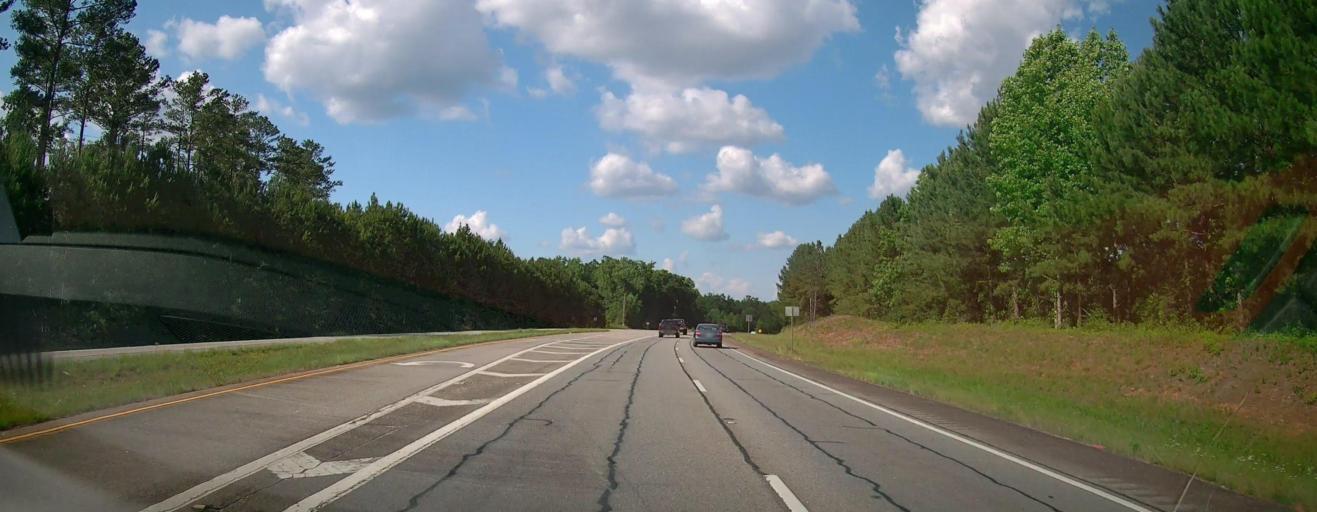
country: US
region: Georgia
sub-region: Henry County
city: Hampton
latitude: 33.3910
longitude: -84.2571
